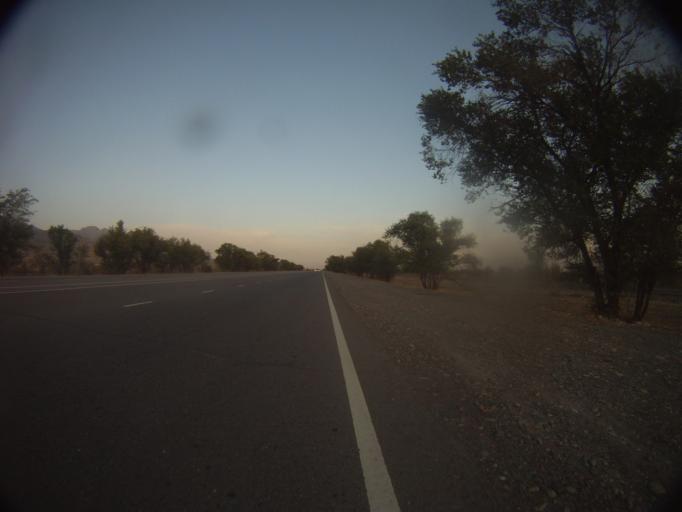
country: KG
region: Chuy
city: Tokmok
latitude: 42.8423
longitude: 75.3855
